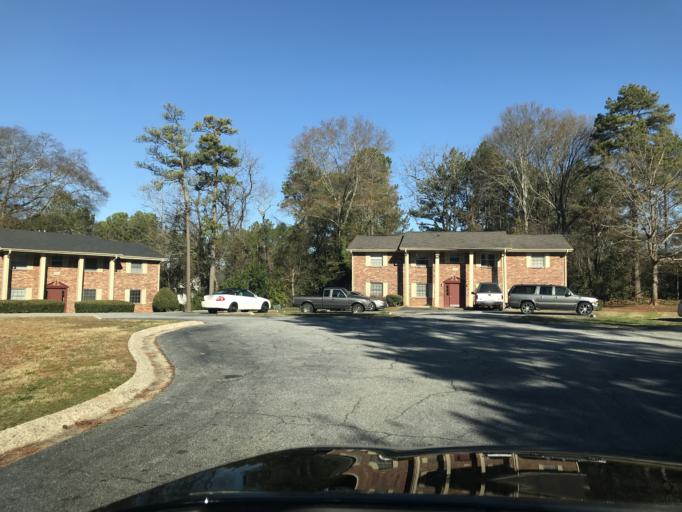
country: US
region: Georgia
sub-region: Clayton County
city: Morrow
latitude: 33.5628
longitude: -84.3733
